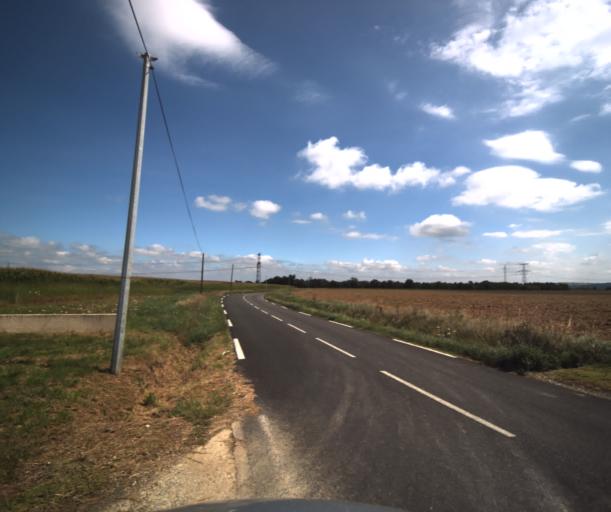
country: FR
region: Midi-Pyrenees
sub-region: Departement de la Haute-Garonne
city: Longages
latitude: 43.3776
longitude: 1.2428
